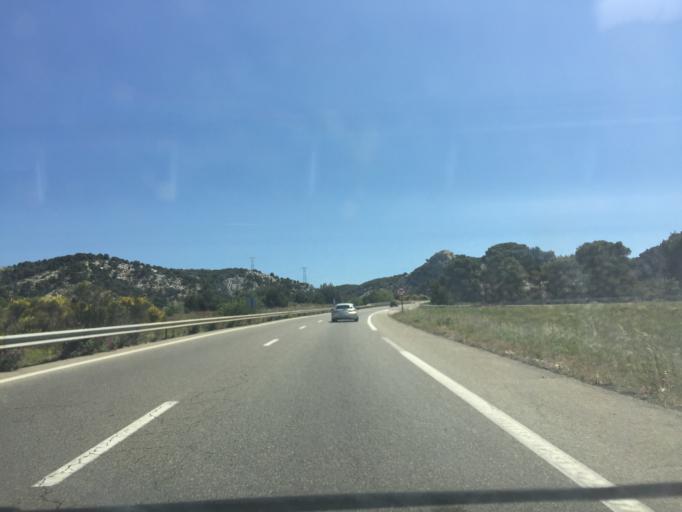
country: FR
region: Provence-Alpes-Cote d'Azur
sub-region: Departement des Bouches-du-Rhone
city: Les Pennes-Mirabeau
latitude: 43.4038
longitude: 5.2969
